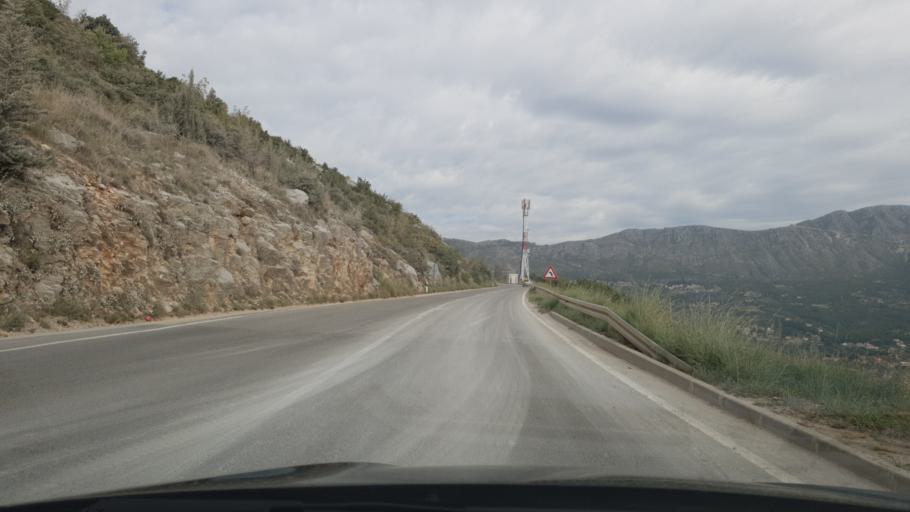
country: HR
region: Dubrovacko-Neretvanska
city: Cibaca
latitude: 42.6335
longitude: 18.1599
